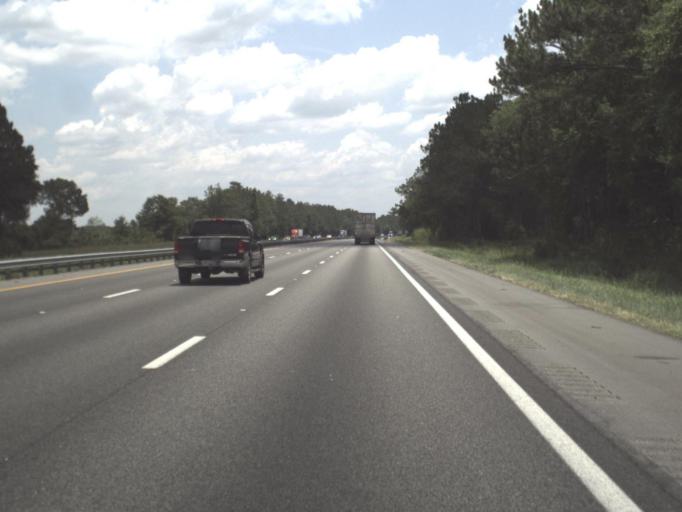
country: US
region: Georgia
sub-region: Echols County
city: Statenville
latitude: 30.5675
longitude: -83.0934
